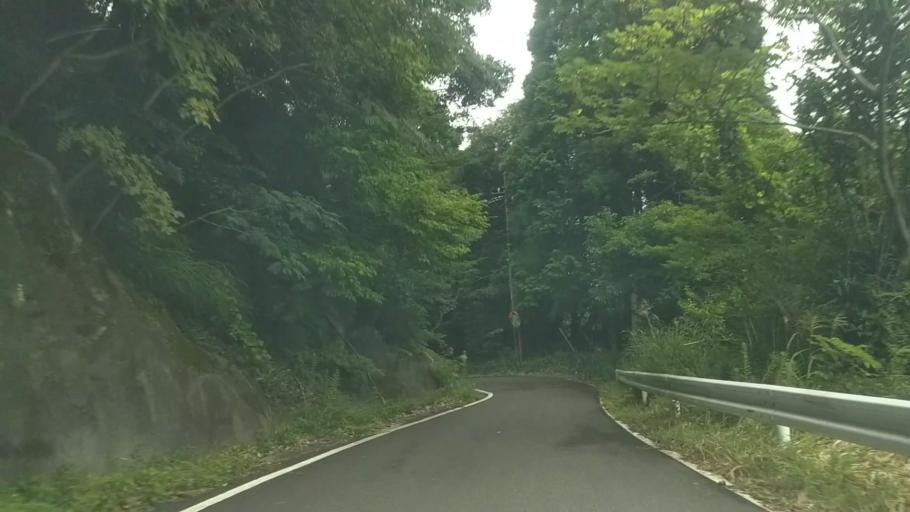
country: JP
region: Chiba
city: Kawaguchi
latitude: 35.2525
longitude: 140.0703
